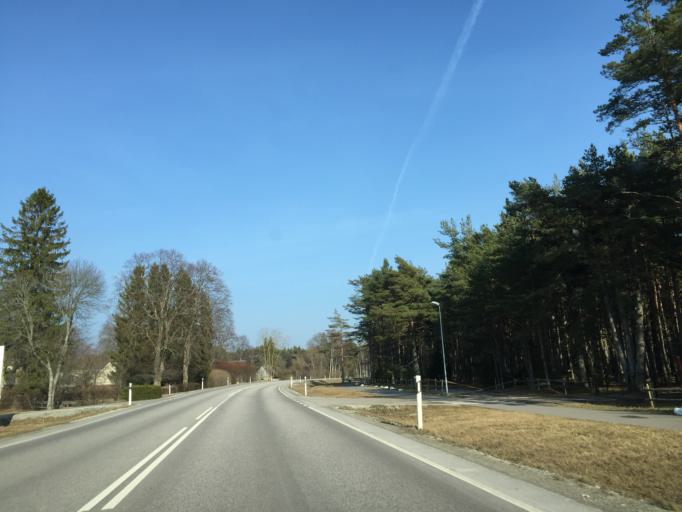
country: EE
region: Saare
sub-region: Kuressaare linn
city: Kuressaare
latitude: 58.2184
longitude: 22.3307
